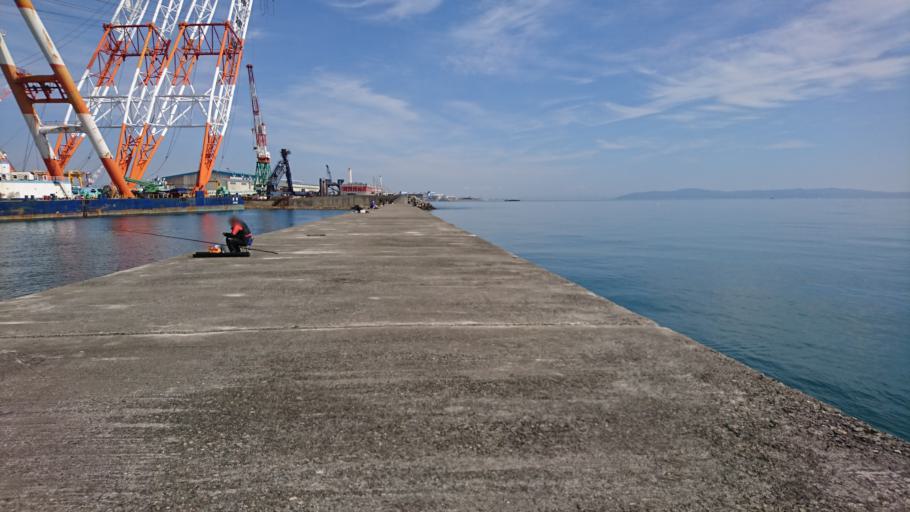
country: JP
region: Hyogo
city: Kakogawacho-honmachi
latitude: 34.6971
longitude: 134.8376
